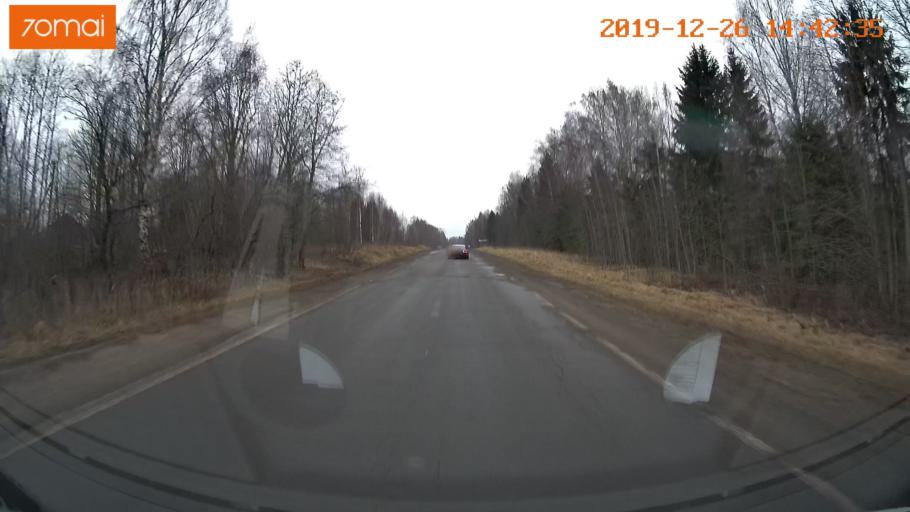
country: RU
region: Jaroslavl
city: Poshekhon'ye
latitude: 58.3630
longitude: 39.0317
